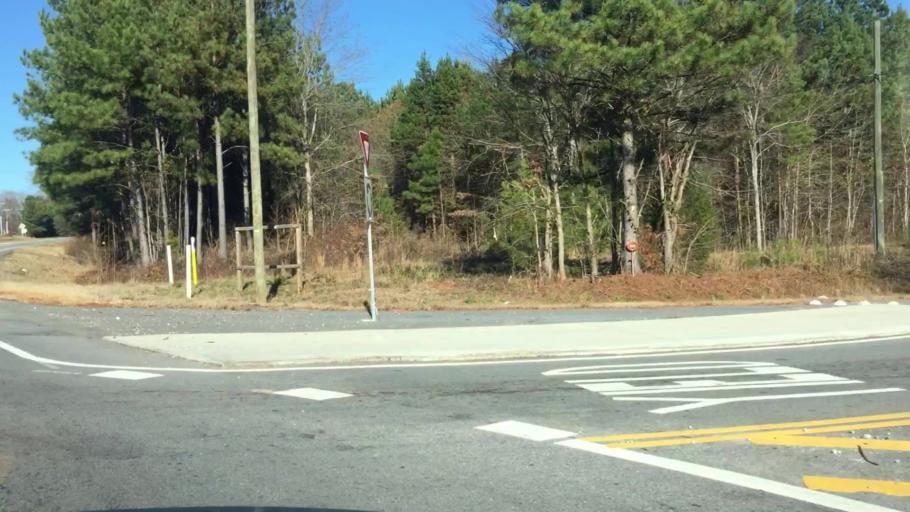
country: US
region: Georgia
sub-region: Newton County
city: Oakwood
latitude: 33.4628
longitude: -83.9685
